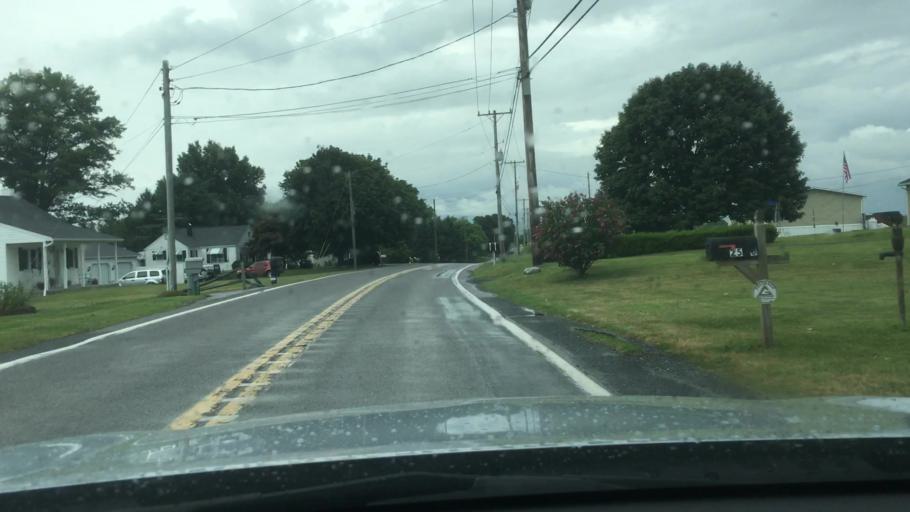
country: US
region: Pennsylvania
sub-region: Franklin County
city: Greencastle
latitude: 39.8760
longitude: -77.7289
